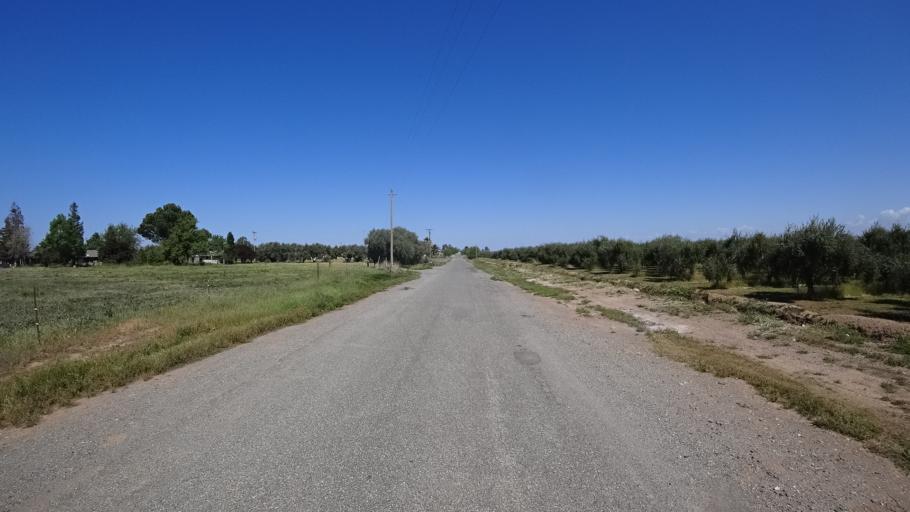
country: US
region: California
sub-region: Glenn County
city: Orland
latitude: 39.7727
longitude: -122.1830
